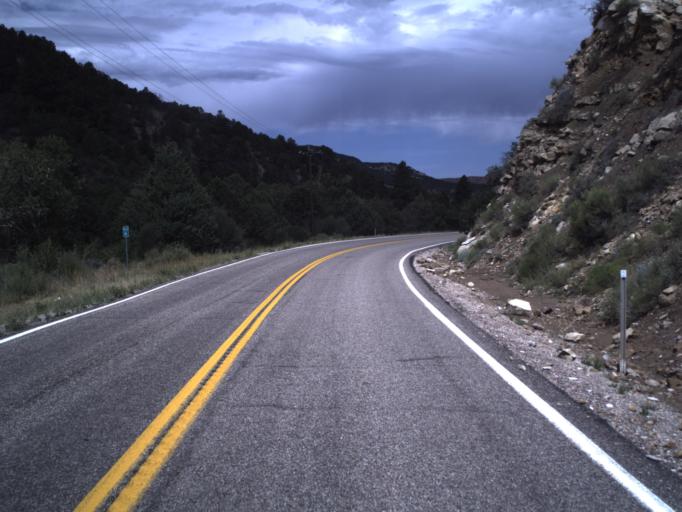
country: US
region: Utah
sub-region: Iron County
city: Cedar City
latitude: 37.6466
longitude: -112.9696
